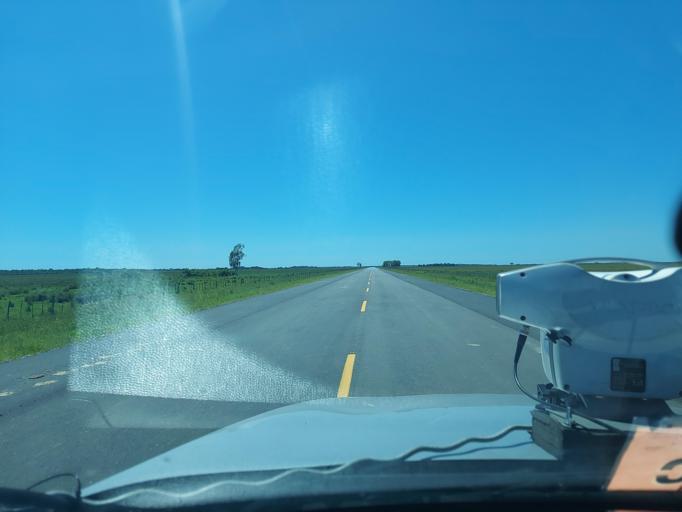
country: PY
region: Neembucu
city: Pilar
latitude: -26.8184
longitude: -58.2545
